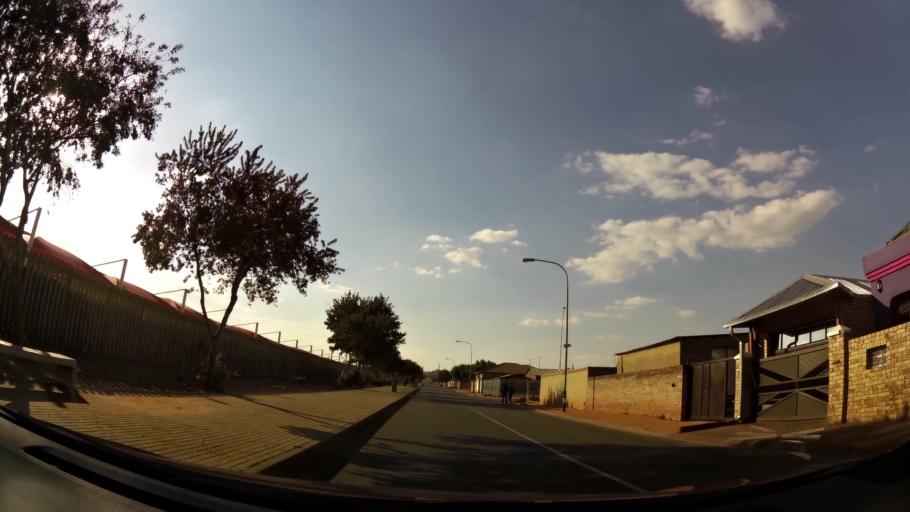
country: ZA
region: Gauteng
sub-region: City of Johannesburg Metropolitan Municipality
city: Roodepoort
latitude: -26.2107
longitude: 27.8770
